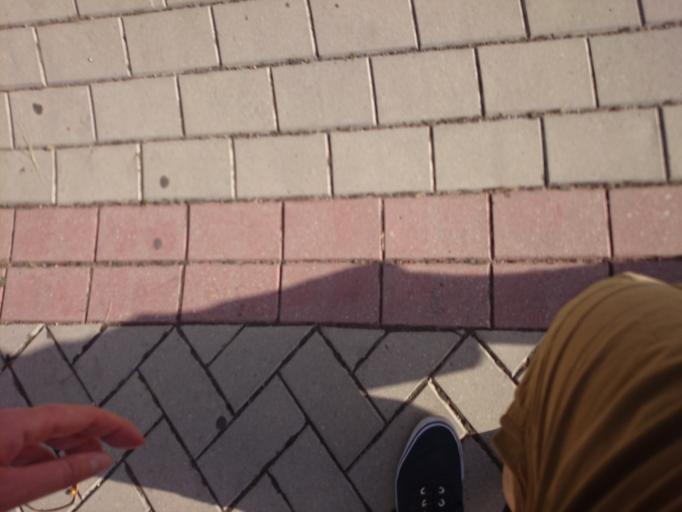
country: ME
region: Kotor
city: Kotor
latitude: 42.4336
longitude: 18.7670
